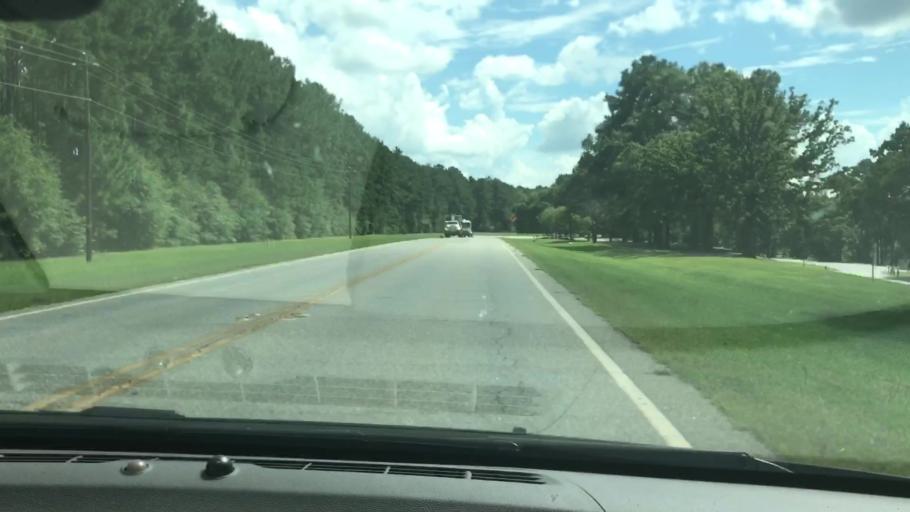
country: US
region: Georgia
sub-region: Clay County
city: Fort Gaines
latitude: 31.6339
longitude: -85.0442
